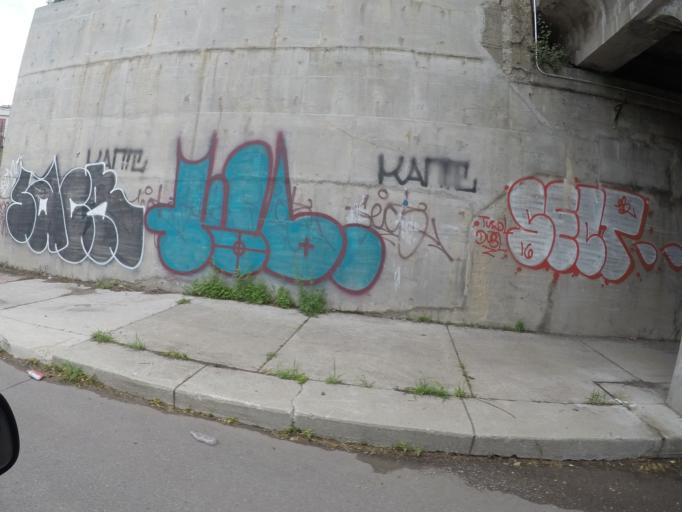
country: US
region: Michigan
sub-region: Wayne County
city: Detroit
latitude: 42.3280
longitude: -83.0793
